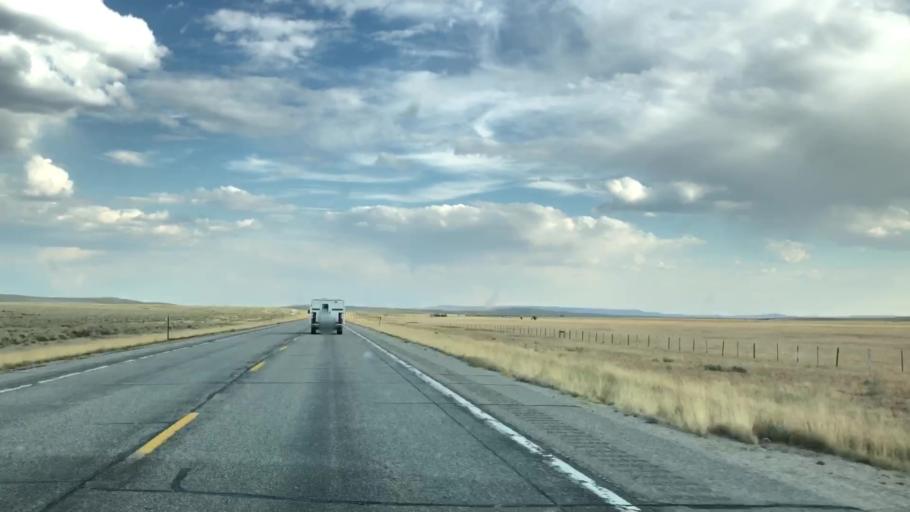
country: US
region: Wyoming
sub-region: Sublette County
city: Pinedale
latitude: 43.0425
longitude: -110.1420
